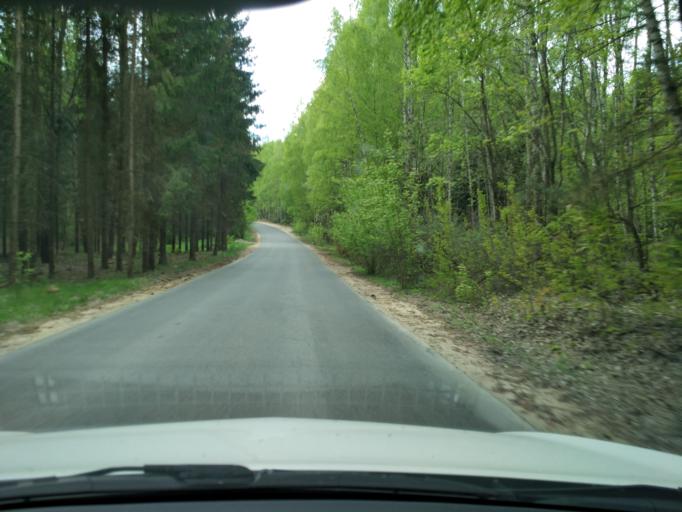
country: LT
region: Vilnius County
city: Rasos
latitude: 54.6942
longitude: 25.3372
